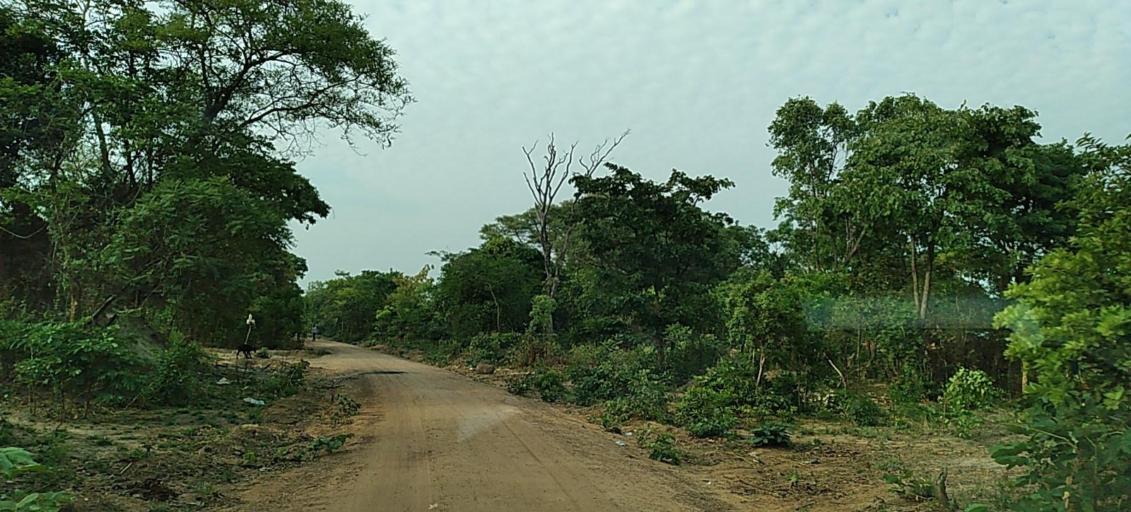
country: ZM
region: Copperbelt
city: Kalulushi
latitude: -12.8896
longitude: 27.6889
